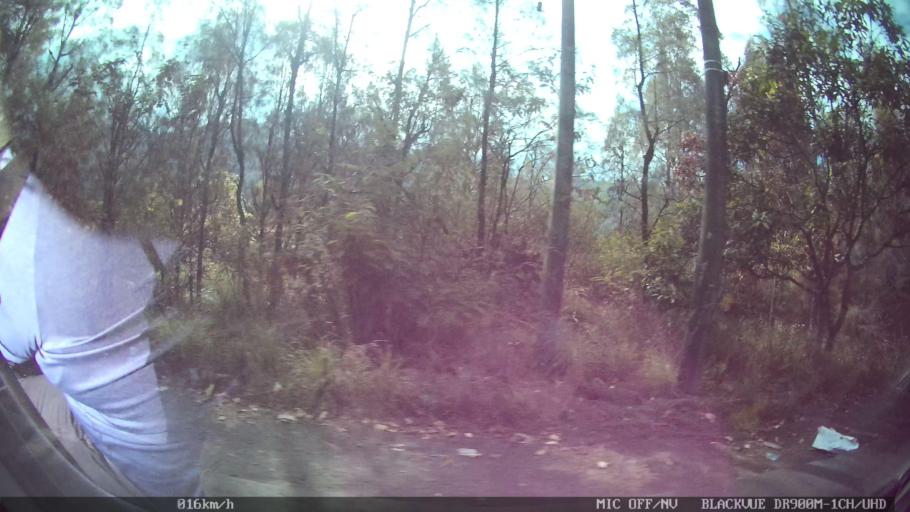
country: ID
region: Bali
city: Banjar Kedisan
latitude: -8.2323
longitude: 115.3568
